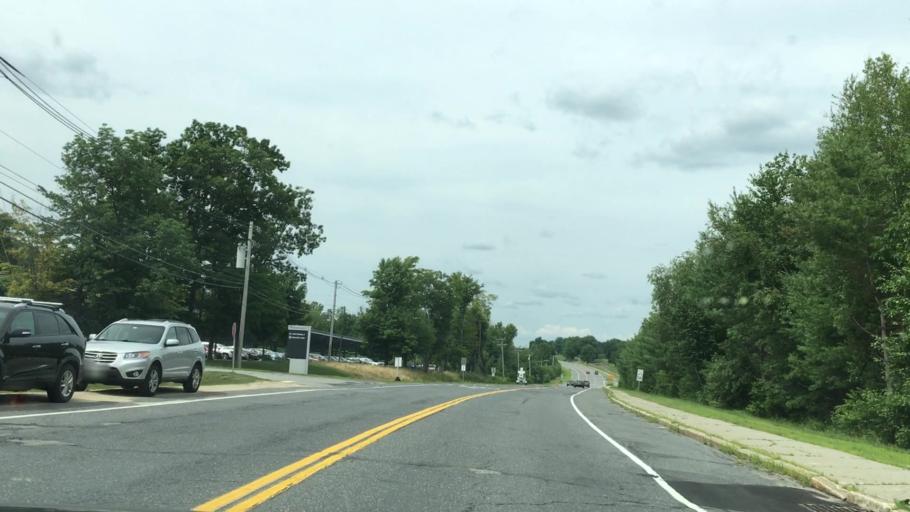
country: US
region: Massachusetts
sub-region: Worcester County
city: Gardner
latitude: 42.5879
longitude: -71.9866
